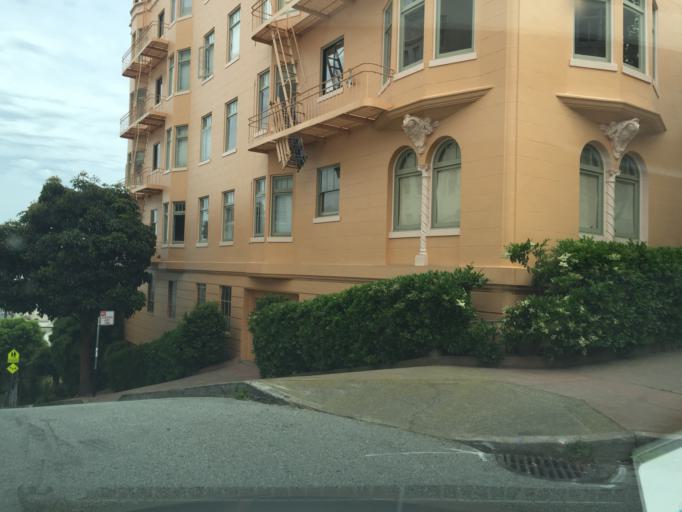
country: US
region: California
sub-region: San Francisco County
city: San Francisco
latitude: 37.8013
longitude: -122.4178
